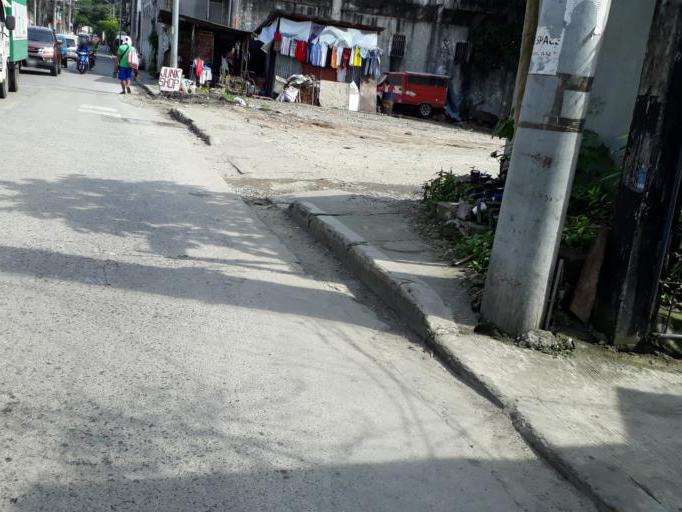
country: PH
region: Calabarzon
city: Bagong Pagasa
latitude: 14.6725
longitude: 121.0054
